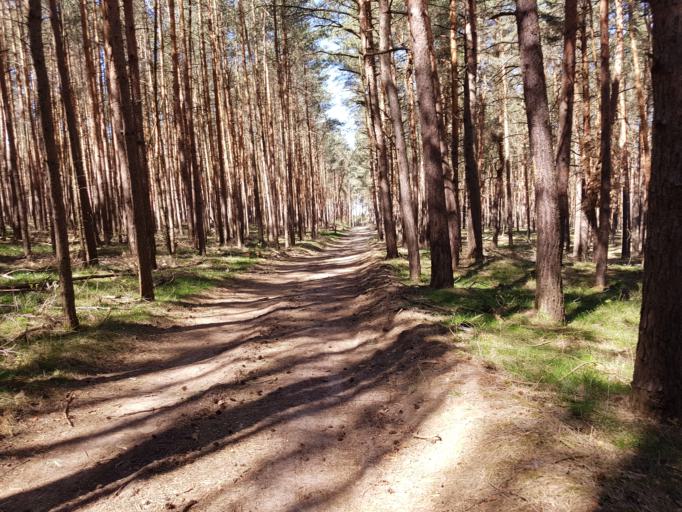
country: DE
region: Brandenburg
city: Groden
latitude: 51.3910
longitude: 13.5761
